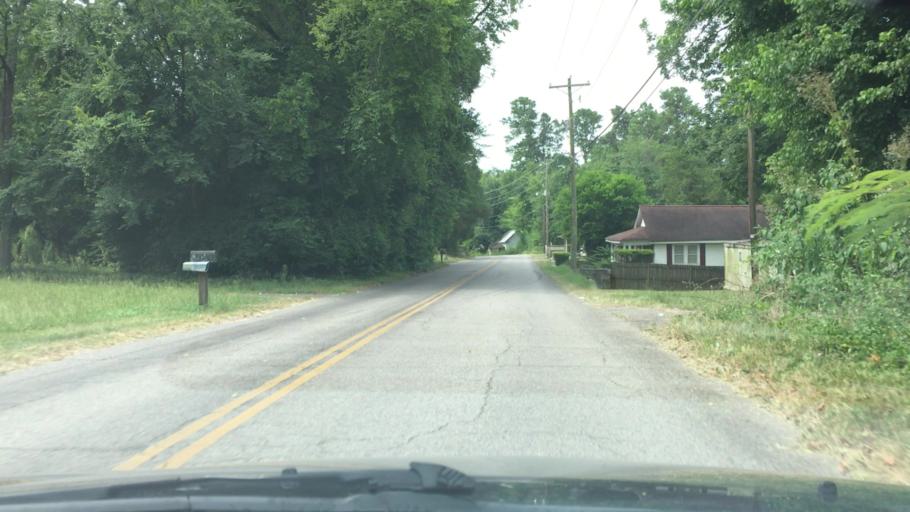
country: US
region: South Carolina
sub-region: Aiken County
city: Graniteville
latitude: 33.5597
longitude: -81.8032
